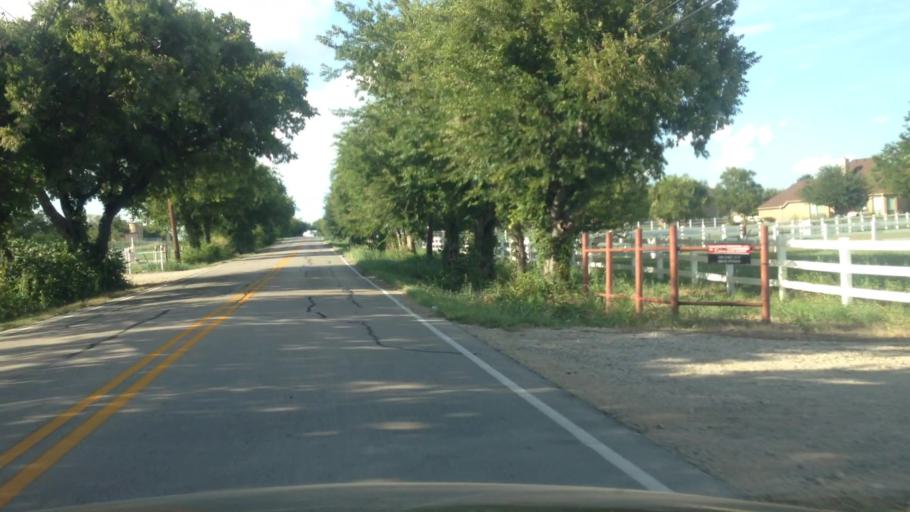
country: US
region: Texas
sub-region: Tarrant County
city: Eagle Mountain
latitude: 32.9287
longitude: -97.3920
